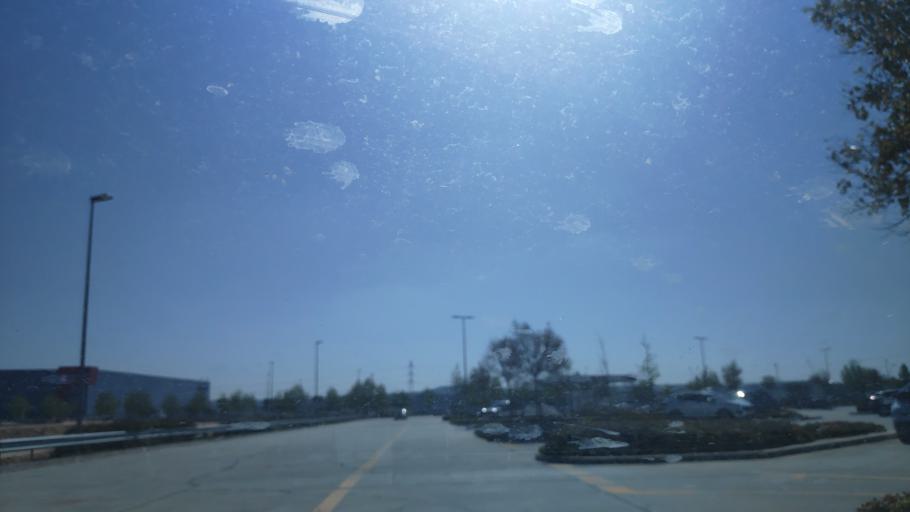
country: ES
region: Madrid
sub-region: Provincia de Madrid
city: Pinto
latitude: 40.2837
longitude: -3.6880
